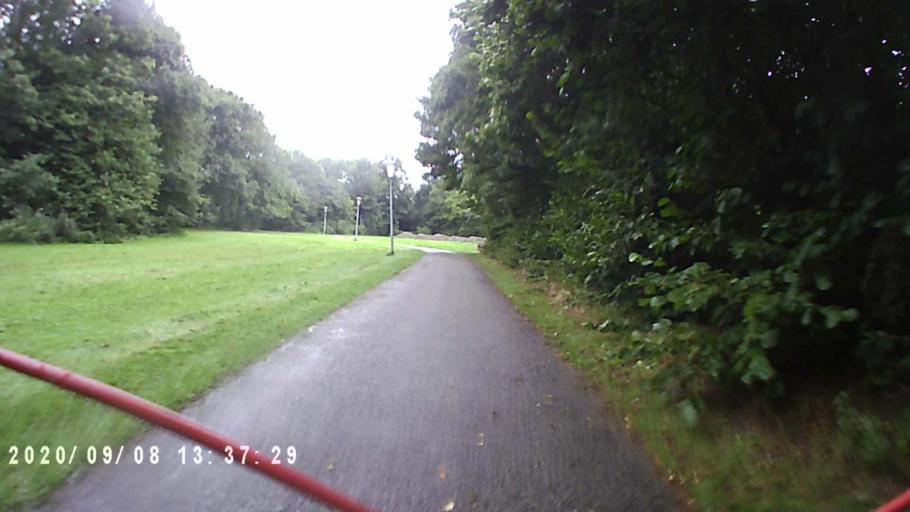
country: NL
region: Groningen
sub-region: Gemeente Veendam
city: Veendam
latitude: 53.1102
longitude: 6.8584
